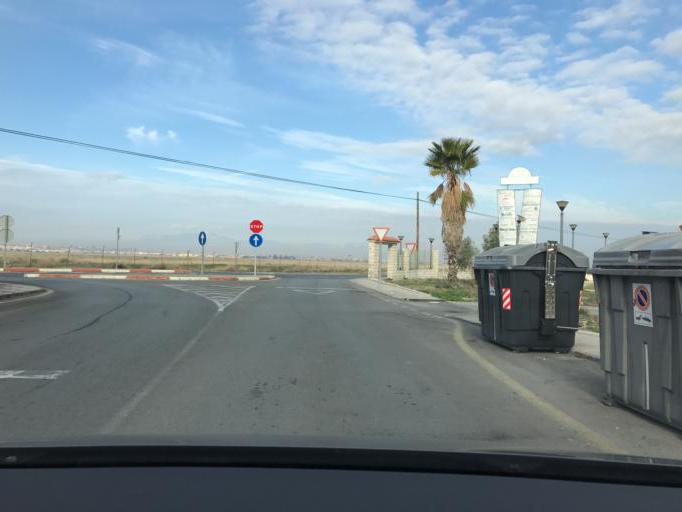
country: ES
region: Andalusia
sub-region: Provincia de Granada
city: Alhendin
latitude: 37.1237
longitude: -3.6308
